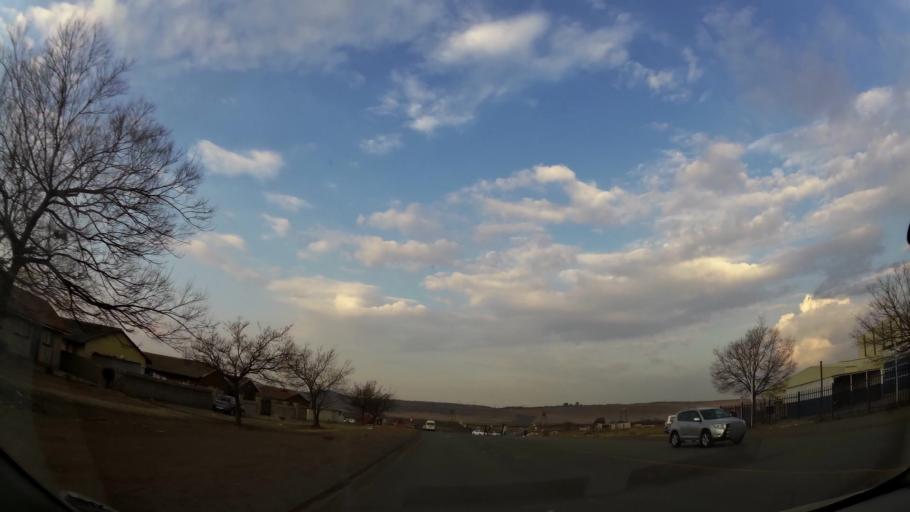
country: ZA
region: Gauteng
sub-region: Sedibeng District Municipality
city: Vereeniging
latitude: -26.5930
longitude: 27.8498
